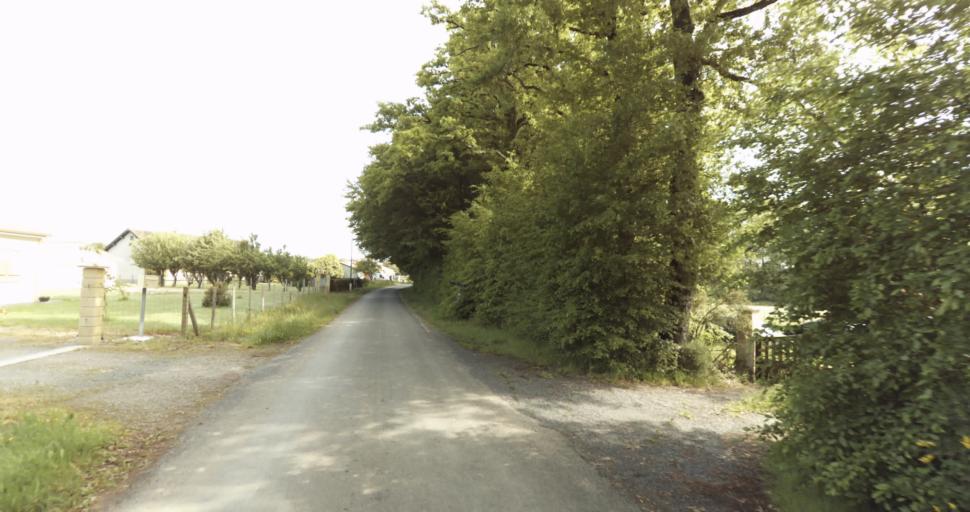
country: FR
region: Limousin
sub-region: Departement de la Haute-Vienne
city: Bosmie-l'Aiguille
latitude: 45.7109
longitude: 1.2343
